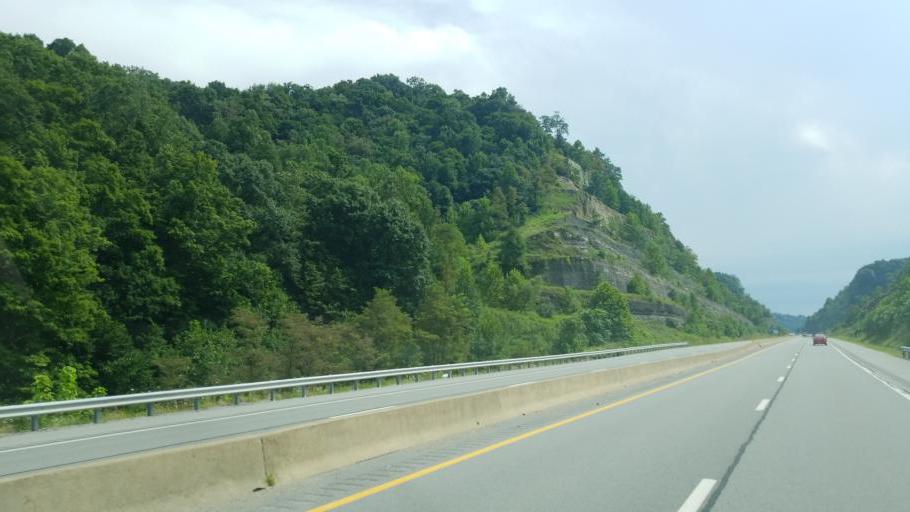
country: US
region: West Virginia
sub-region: Logan County
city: Mount Gay-Shamrock
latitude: 37.8968
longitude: -82.0447
